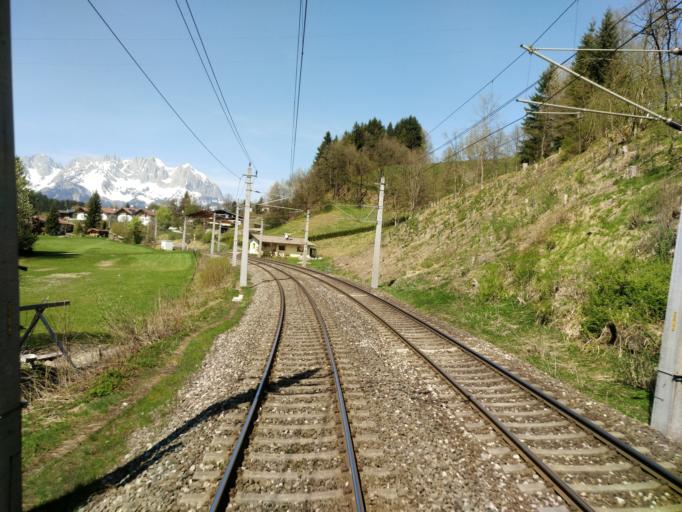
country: AT
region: Tyrol
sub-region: Politischer Bezirk Kitzbuhel
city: Kitzbuhel
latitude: 47.4627
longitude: 12.3891
